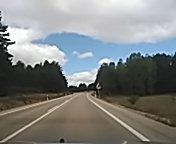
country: ES
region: Castille and Leon
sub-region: Provincia de Soria
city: San Leonardo de Yague
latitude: 41.8398
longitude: -3.0946
